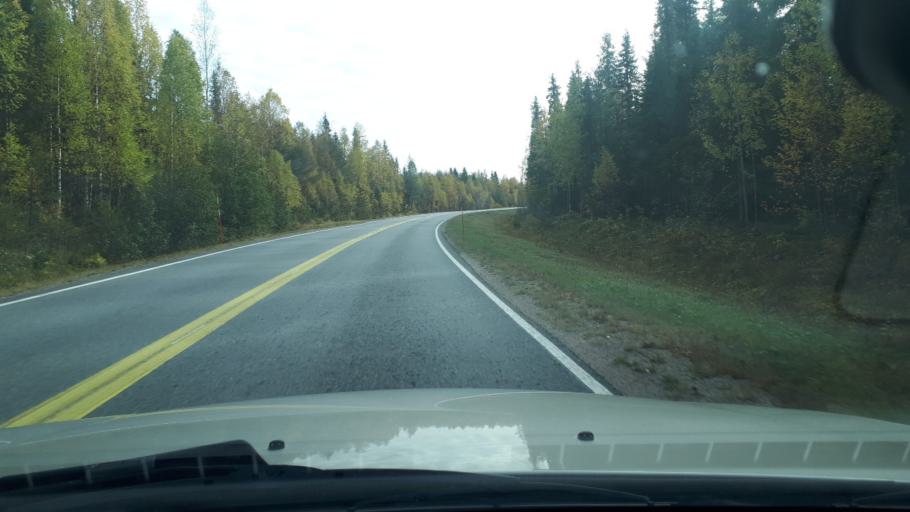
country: FI
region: Lapland
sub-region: Rovaniemi
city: Ranua
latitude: 65.9679
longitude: 26.0141
